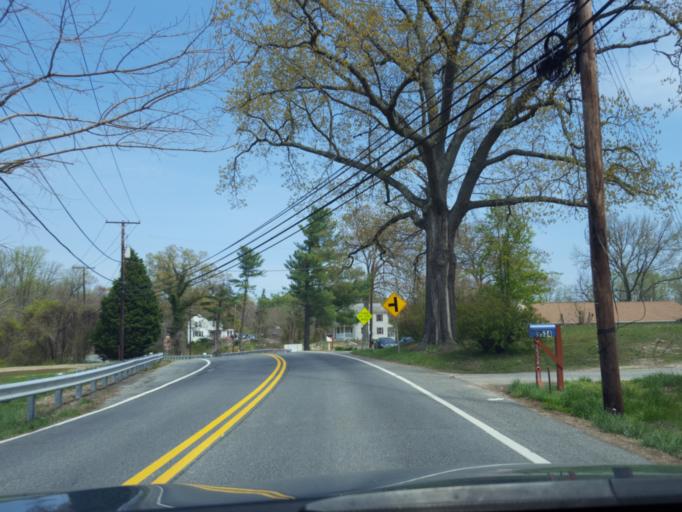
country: US
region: Maryland
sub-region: Prince George's County
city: Croom
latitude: 38.7583
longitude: -76.7615
